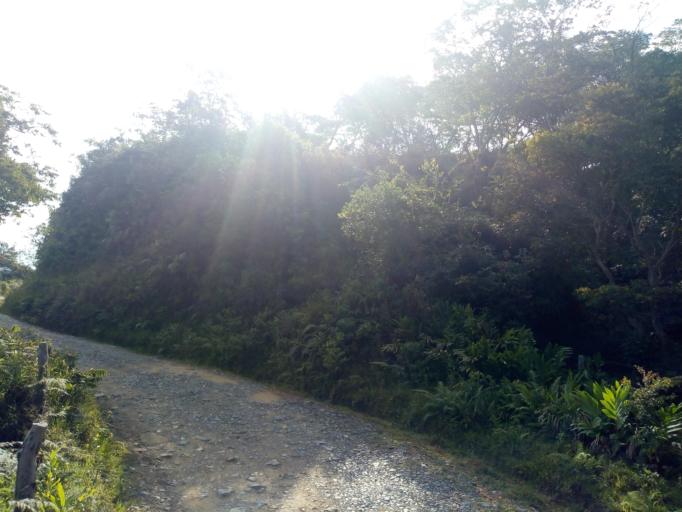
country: CO
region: Boyaca
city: Moniquira
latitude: 5.8852
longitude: -73.5154
